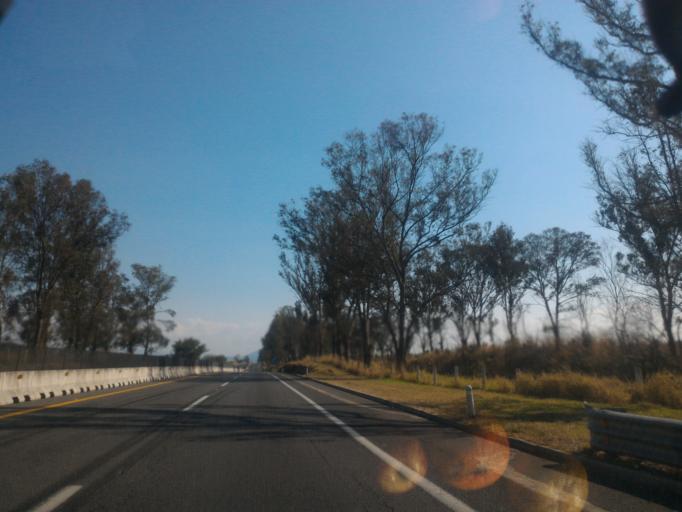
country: MX
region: Jalisco
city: Zapotiltic
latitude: 19.6199
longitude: -103.4620
